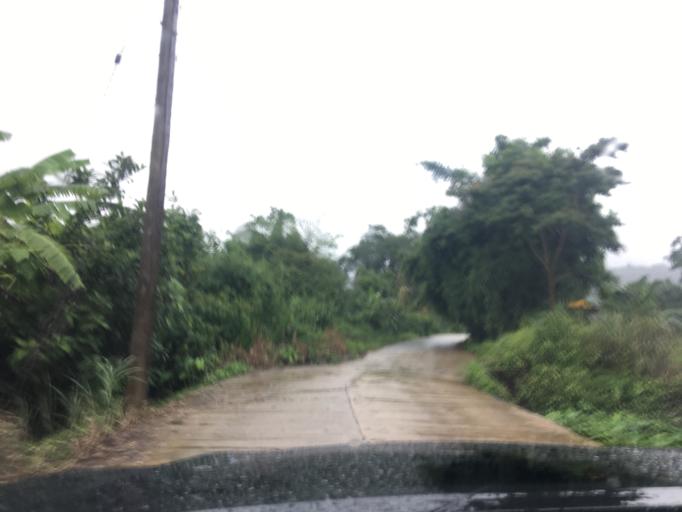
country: TH
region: Chiang Rai
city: Chiang Khong
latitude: 20.2991
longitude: 100.2547
